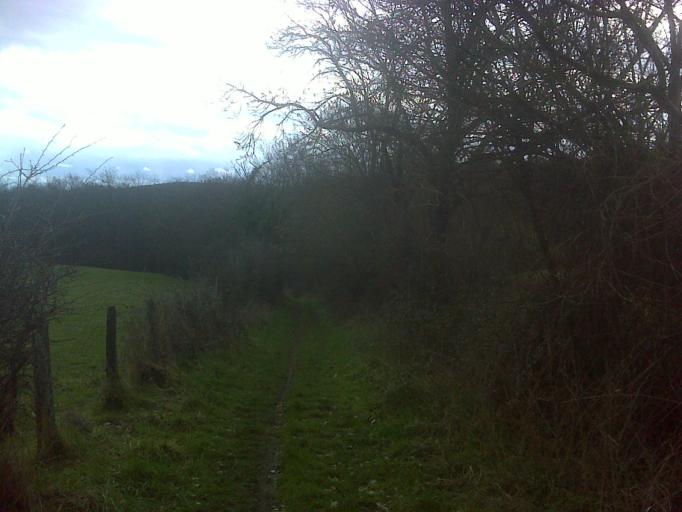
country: FR
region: Rhone-Alpes
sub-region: Departement du Rhone
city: Lentilly
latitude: 45.8092
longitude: 4.6453
